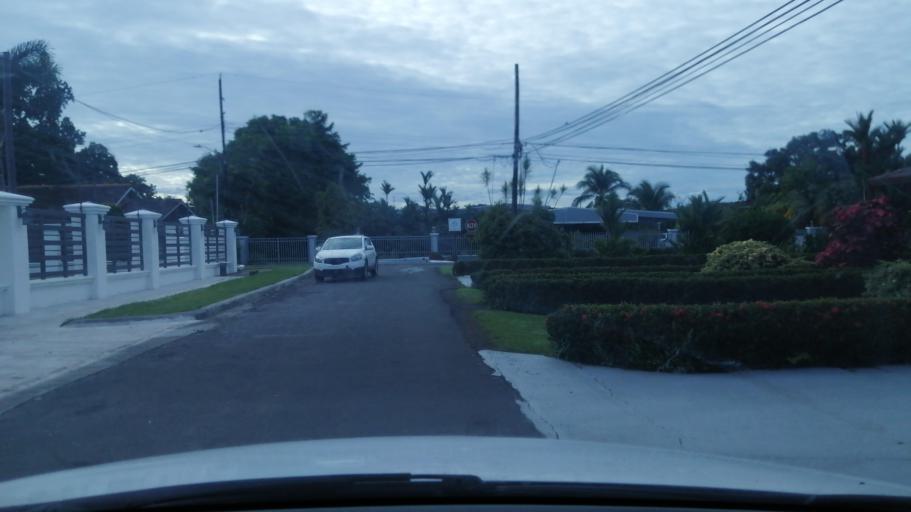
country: PA
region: Chiriqui
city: Mata del Nance
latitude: 8.4568
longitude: -82.4152
